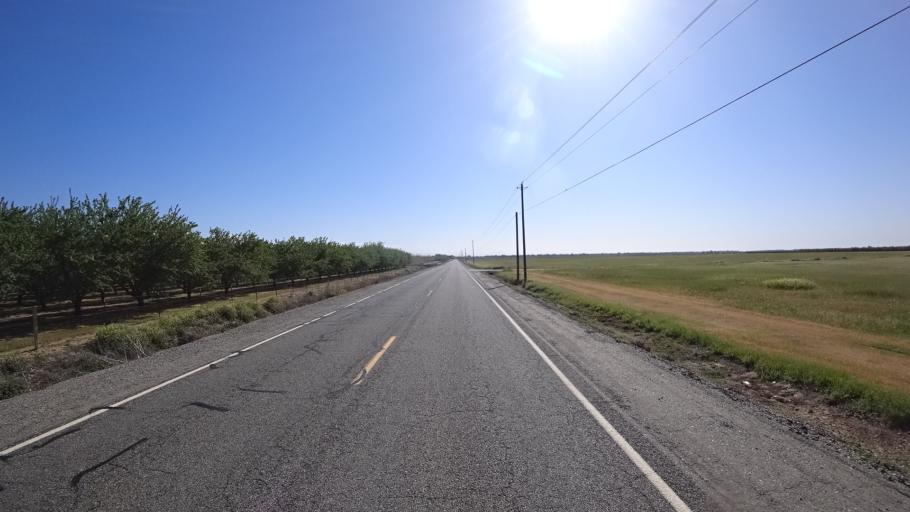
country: US
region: California
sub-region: Glenn County
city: Hamilton City
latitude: 39.7091
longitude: -122.0277
